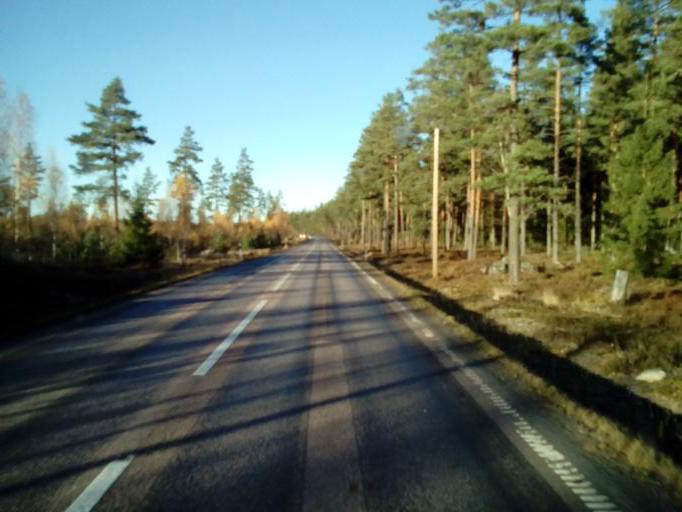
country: SE
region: OErebro
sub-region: Hallsbergs Kommun
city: Palsboda
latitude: 58.8472
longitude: 15.4041
